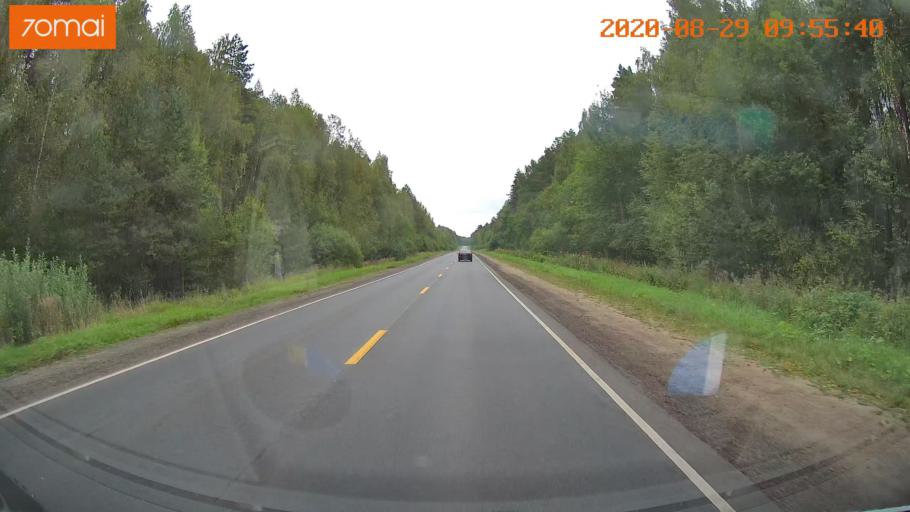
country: RU
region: Ivanovo
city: Zarechnyy
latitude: 57.4219
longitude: 42.2694
